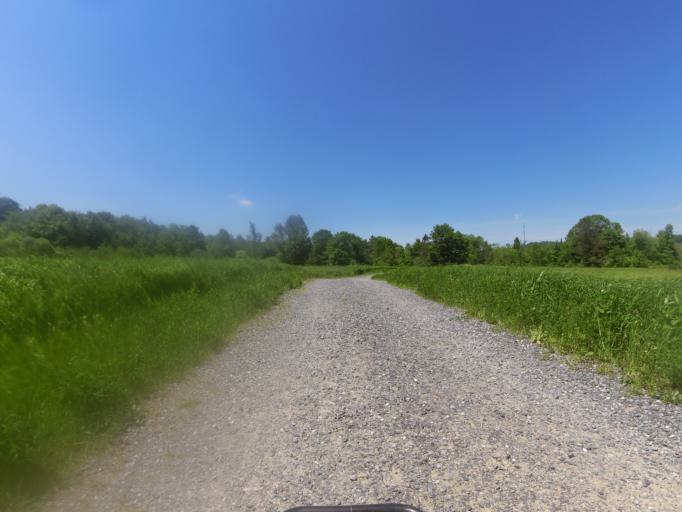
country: CA
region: Quebec
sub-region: Outaouais
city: Wakefield
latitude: 45.6287
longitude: -75.9413
